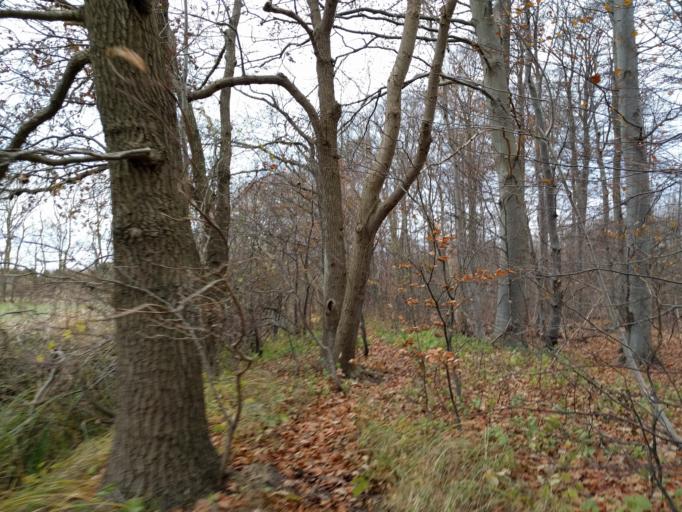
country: DK
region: South Denmark
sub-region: Kerteminde Kommune
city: Langeskov
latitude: 55.4013
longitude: 10.5637
